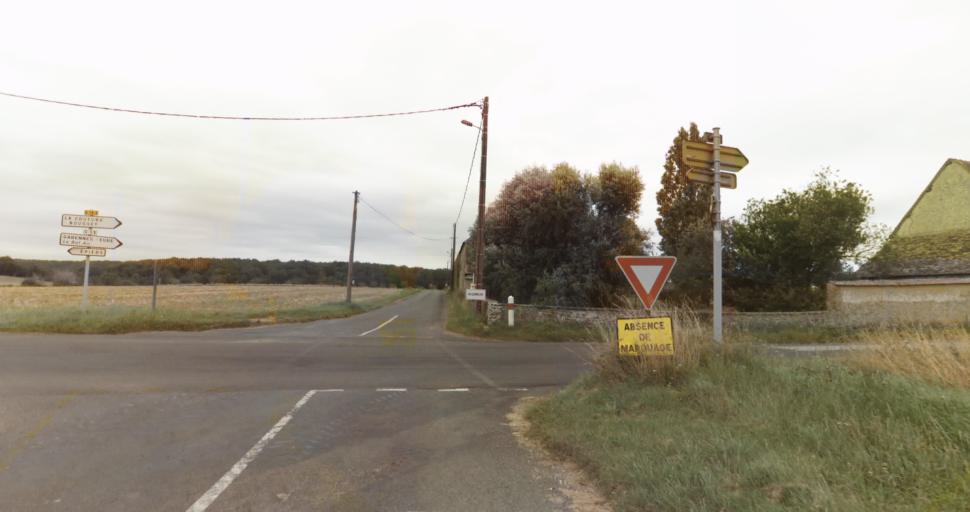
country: FR
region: Haute-Normandie
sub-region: Departement de l'Eure
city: La Couture-Boussey
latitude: 48.9093
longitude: 1.4075
